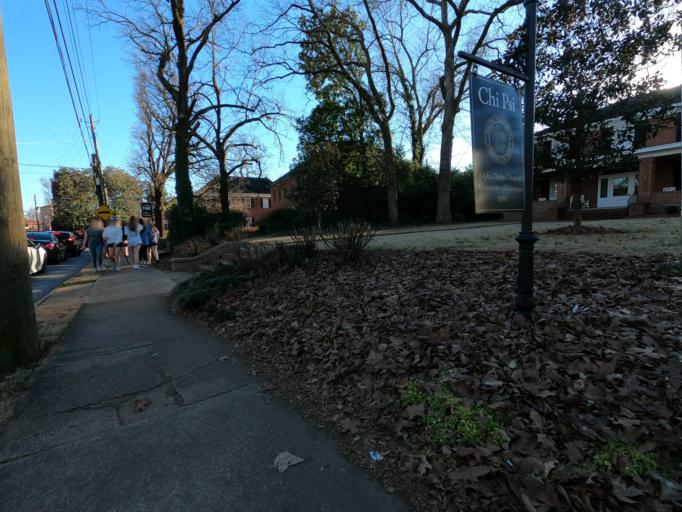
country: US
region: Georgia
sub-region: Clarke County
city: Athens
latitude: 33.9408
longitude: -83.3875
